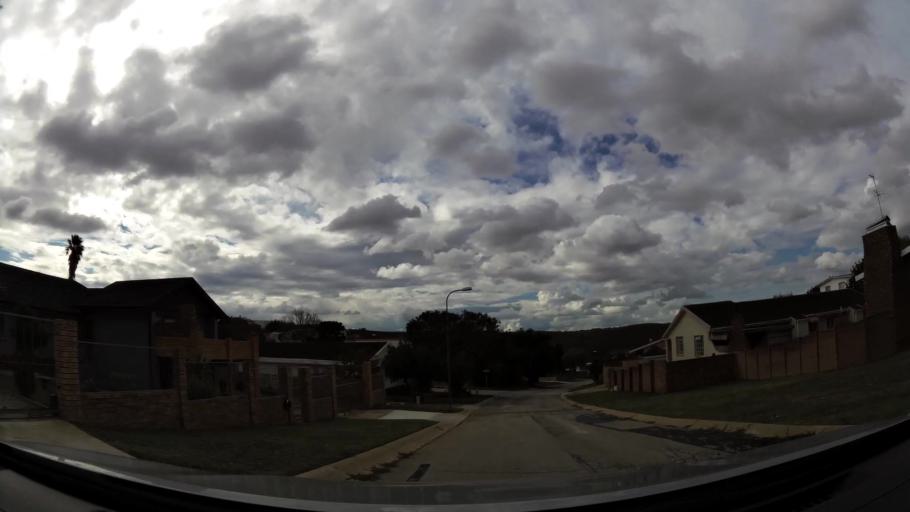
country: ZA
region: Eastern Cape
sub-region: Nelson Mandela Bay Metropolitan Municipality
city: Port Elizabeth
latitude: -33.9329
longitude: 25.5197
